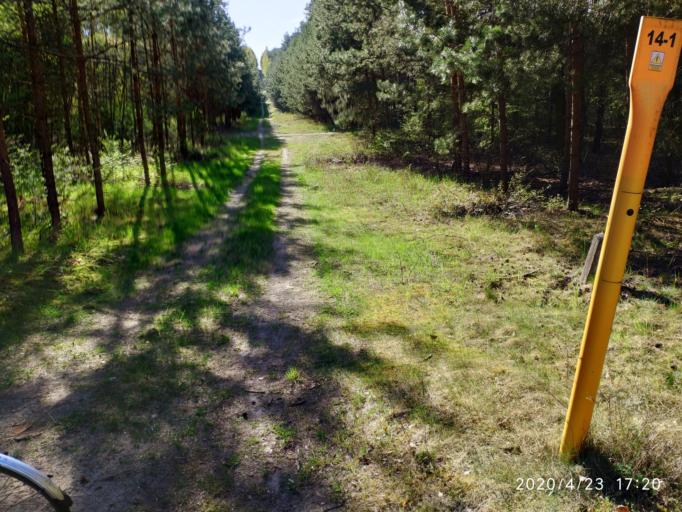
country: PL
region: Lubusz
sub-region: Powiat slubicki
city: Osno Lubuskie
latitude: 52.4738
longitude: 14.8705
